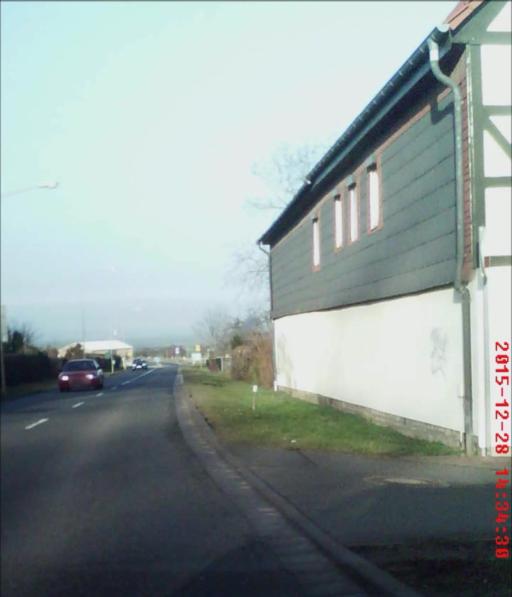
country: DE
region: Thuringia
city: Grossobringen
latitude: 51.0327
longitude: 11.3360
